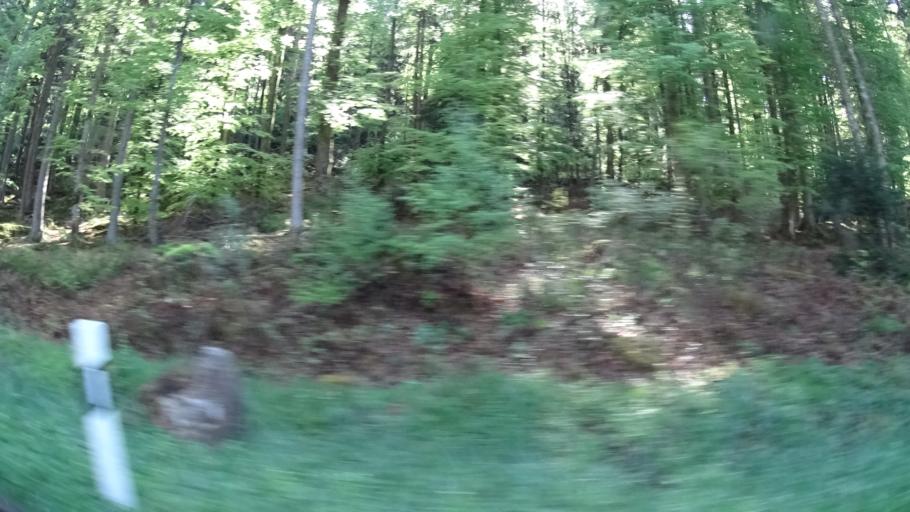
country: DE
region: Baden-Wuerttemberg
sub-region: Karlsruhe Region
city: Bad Wildbad
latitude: 48.7405
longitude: 8.5785
